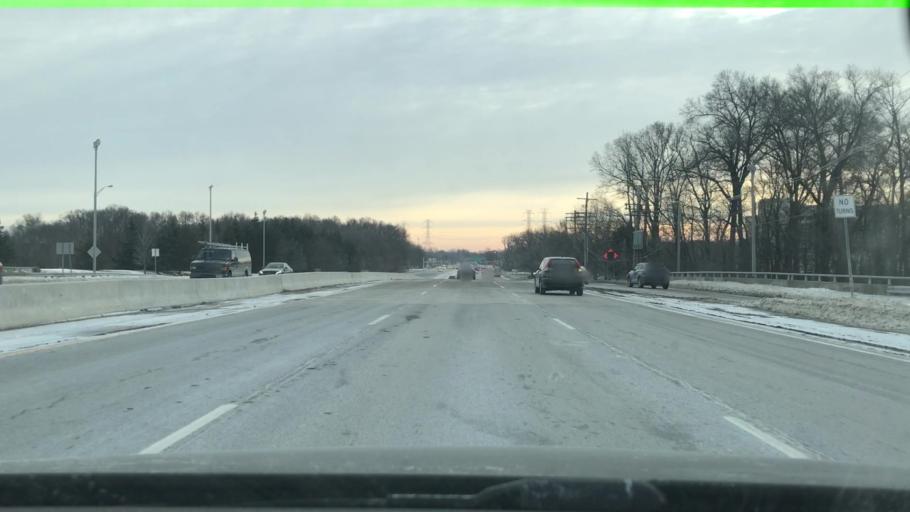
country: US
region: New Jersey
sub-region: Morris County
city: Parsippany
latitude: 40.8384
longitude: -74.4516
